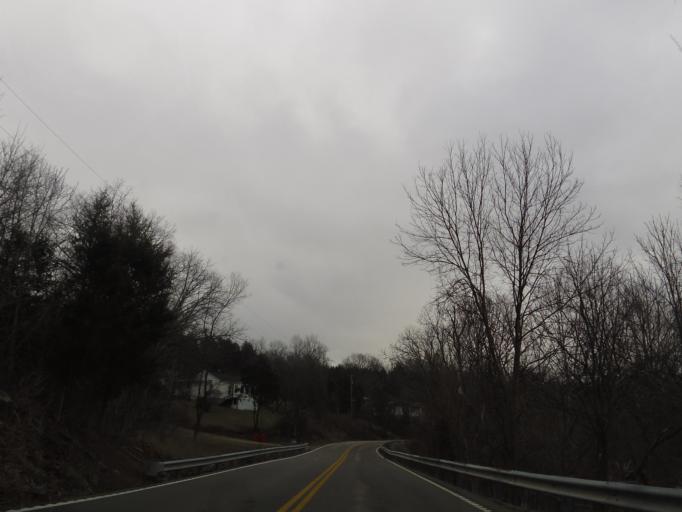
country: US
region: Kentucky
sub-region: Franklin County
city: Frankfort
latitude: 38.2505
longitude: -84.9303
